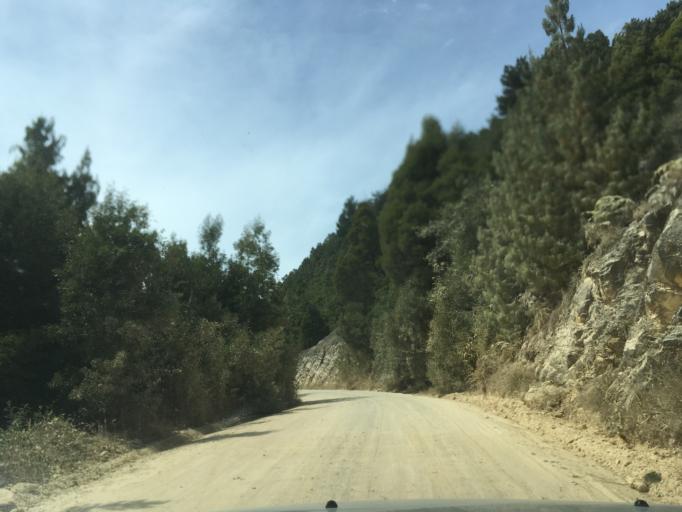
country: CO
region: Boyaca
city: Aquitania
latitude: 5.5752
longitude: -72.9341
